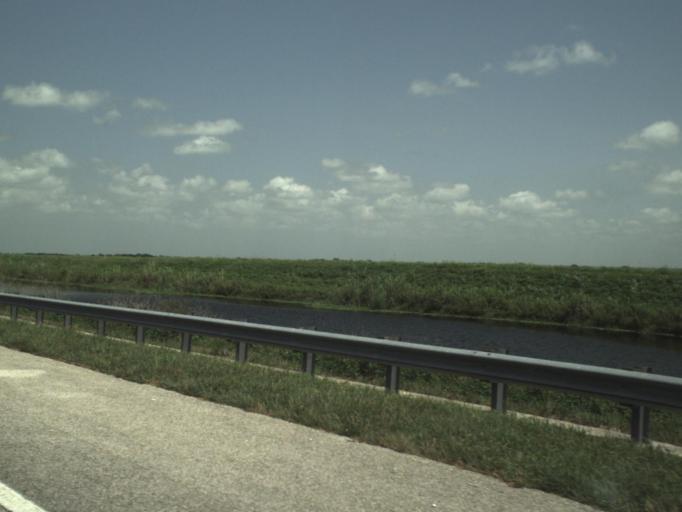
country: US
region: Florida
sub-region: Palm Beach County
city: Belle Glade Camp
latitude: 26.5241
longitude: -80.6842
